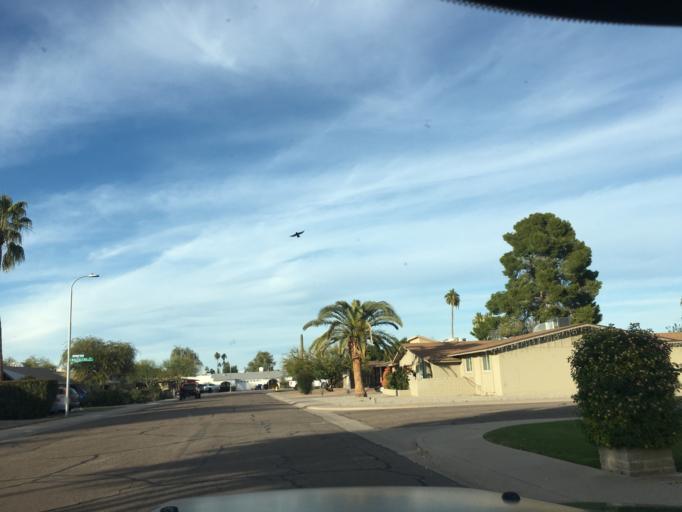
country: US
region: Arizona
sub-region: Maricopa County
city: Tempe
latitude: 33.3697
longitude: -111.9094
